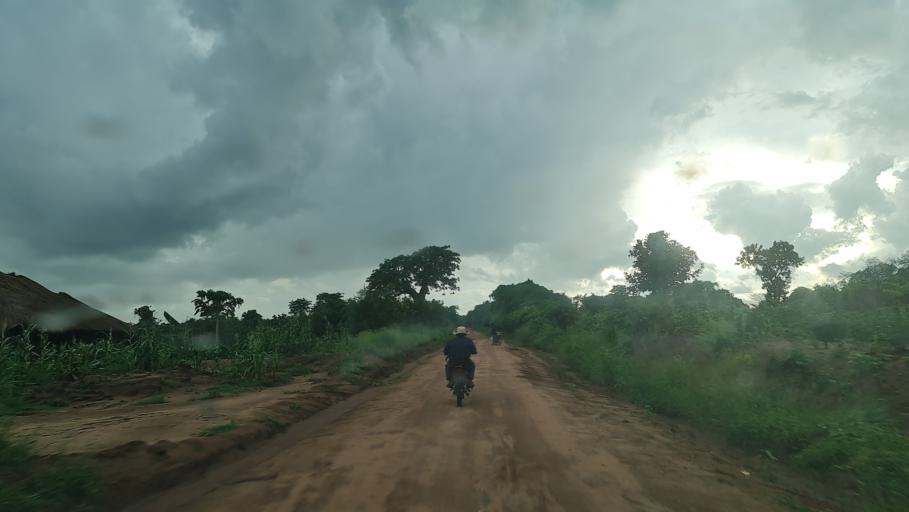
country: MZ
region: Nampula
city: Nacala
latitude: -13.9941
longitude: 40.3666
